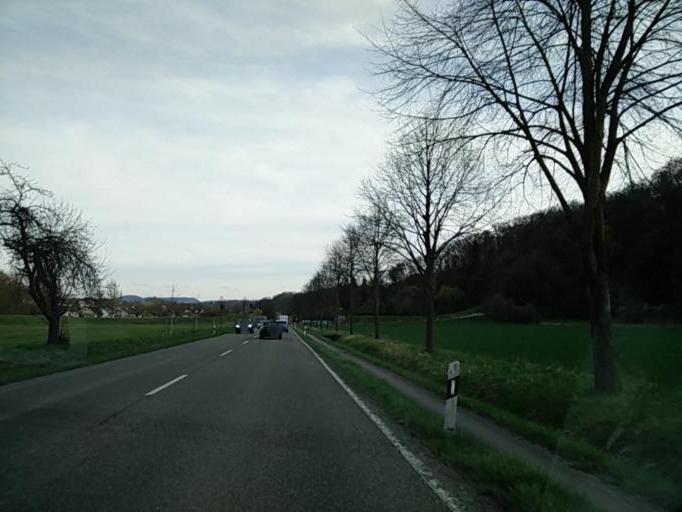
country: DE
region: Baden-Wuerttemberg
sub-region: Tuebingen Region
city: Tuebingen
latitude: 48.5382
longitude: 9.0767
